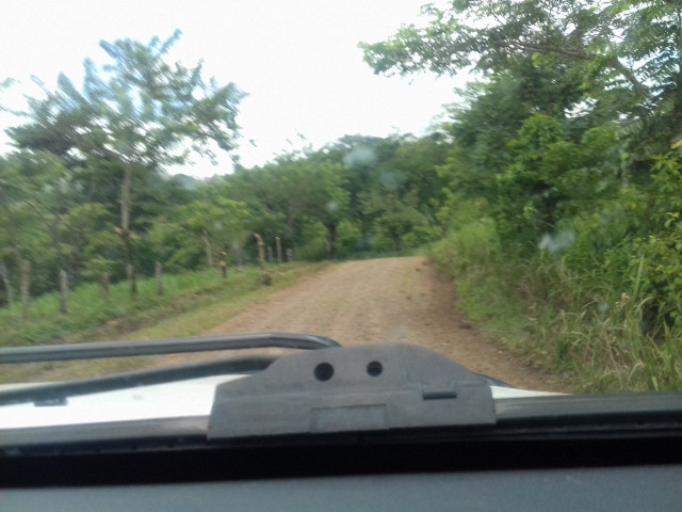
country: NI
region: Matagalpa
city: Matiguas
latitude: 13.0205
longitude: -85.4192
